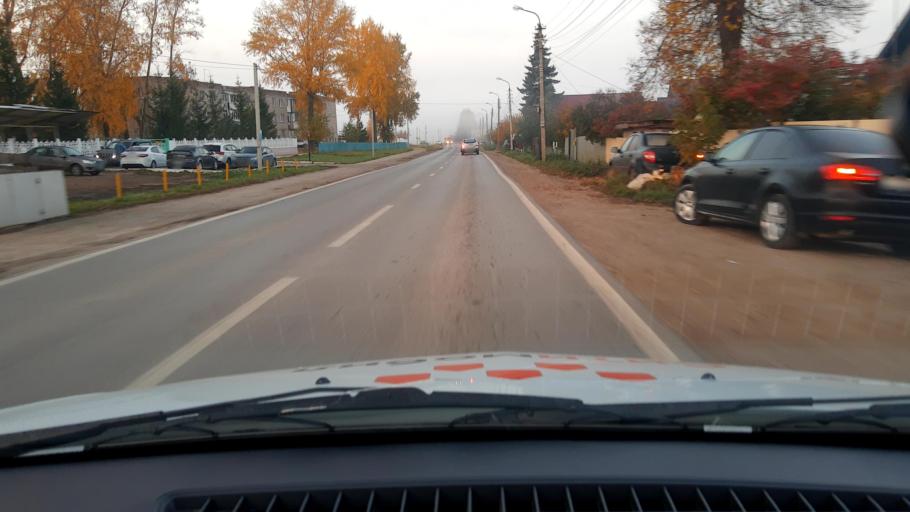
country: RU
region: Bashkortostan
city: Iglino
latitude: 54.7903
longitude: 56.2352
